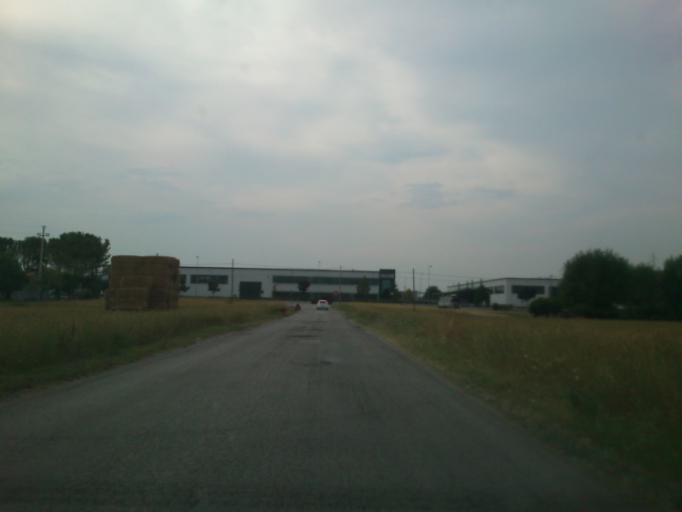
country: IT
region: The Marches
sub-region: Provincia di Pesaro e Urbino
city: Lucrezia
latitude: 43.7657
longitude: 12.9583
